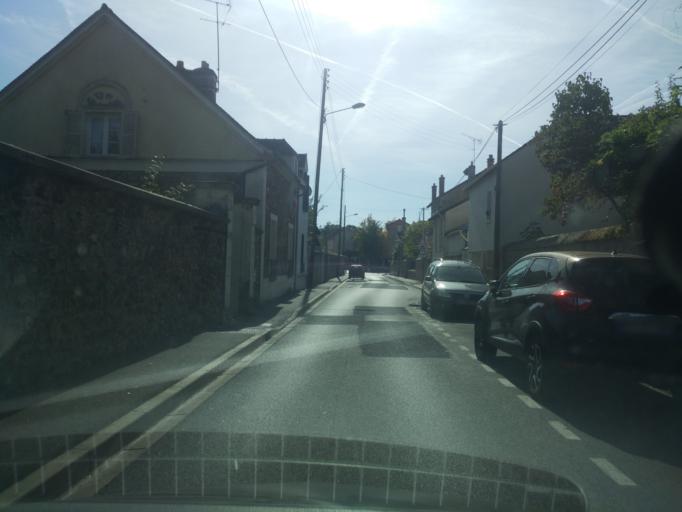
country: FR
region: Ile-de-France
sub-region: Departement de l'Essonne
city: Limours
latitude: 48.6479
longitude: 2.0749
